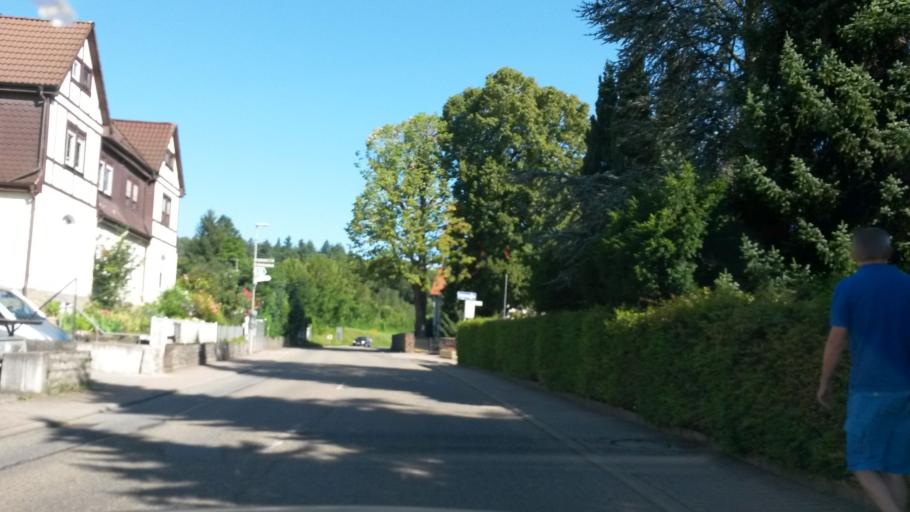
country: DE
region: Baden-Wuerttemberg
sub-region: Karlsruhe Region
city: Konigsbach-Stein
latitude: 48.9503
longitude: 8.6200
